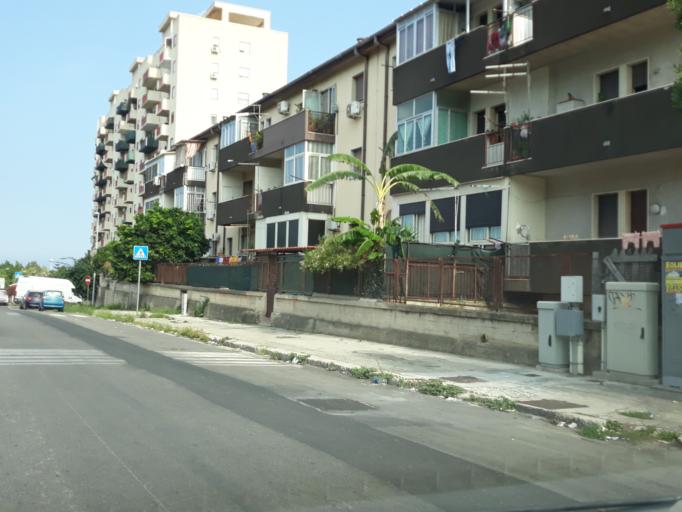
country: IT
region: Sicily
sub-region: Palermo
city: Villa Ciambra
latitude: 38.0858
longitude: 13.3591
